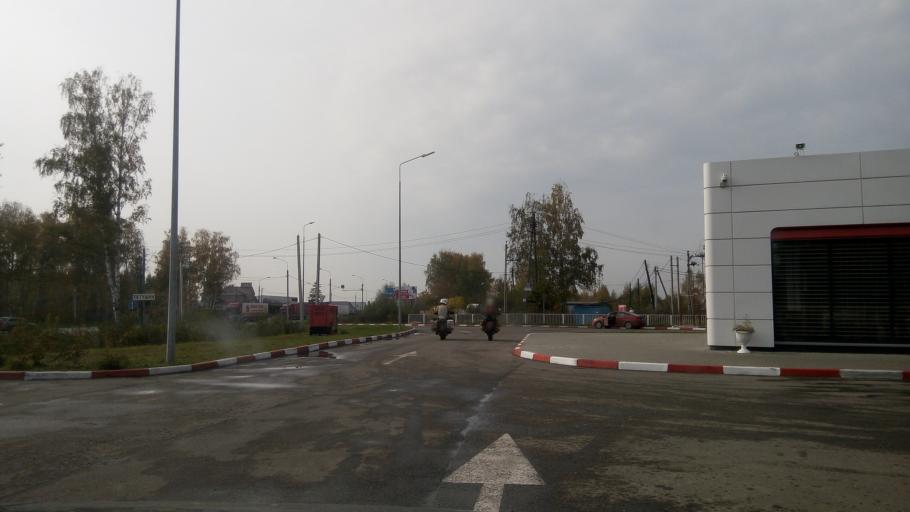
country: RU
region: Vladimir
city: Petushki
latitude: 55.9444
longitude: 39.5010
